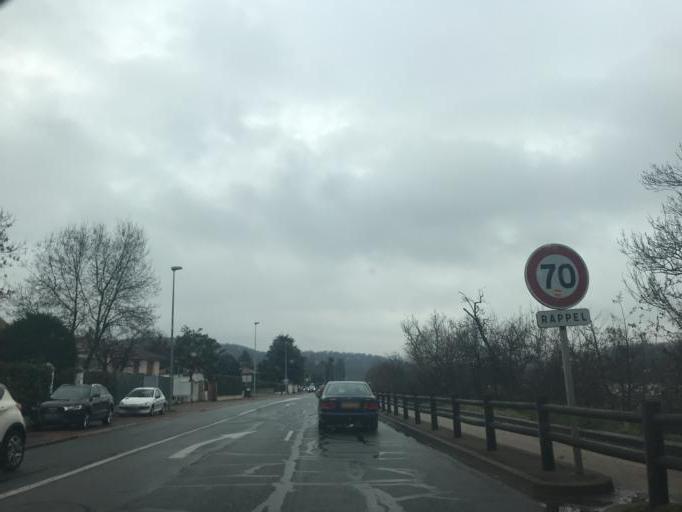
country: FR
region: Rhone-Alpes
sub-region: Departement du Rhone
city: Fleurieu-sur-Saone
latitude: 45.8651
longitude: 4.8399
